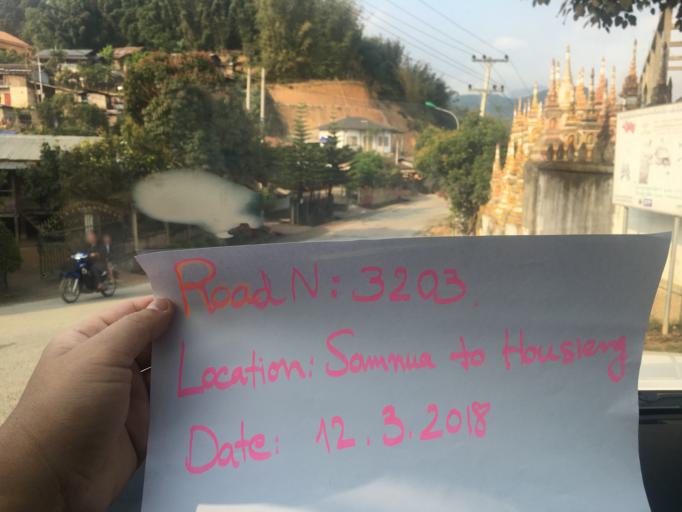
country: LA
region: Houaphan
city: Xam Nua
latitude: 20.4238
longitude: 104.0415
